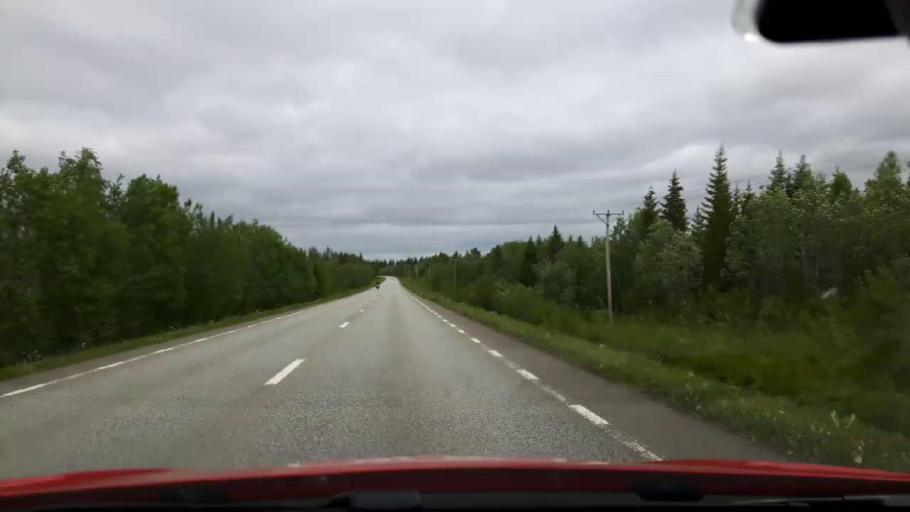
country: SE
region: Jaemtland
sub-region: Krokoms Kommun
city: Krokom
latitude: 63.5669
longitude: 14.6175
